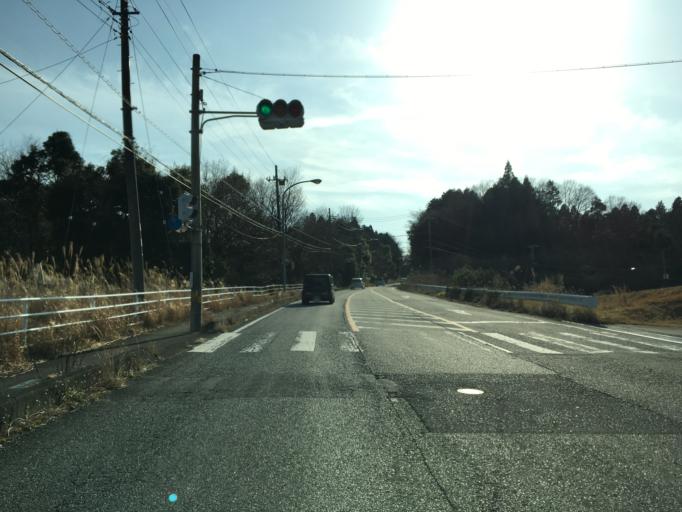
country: JP
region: Ibaraki
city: Takahagi
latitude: 36.7323
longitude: 140.6864
